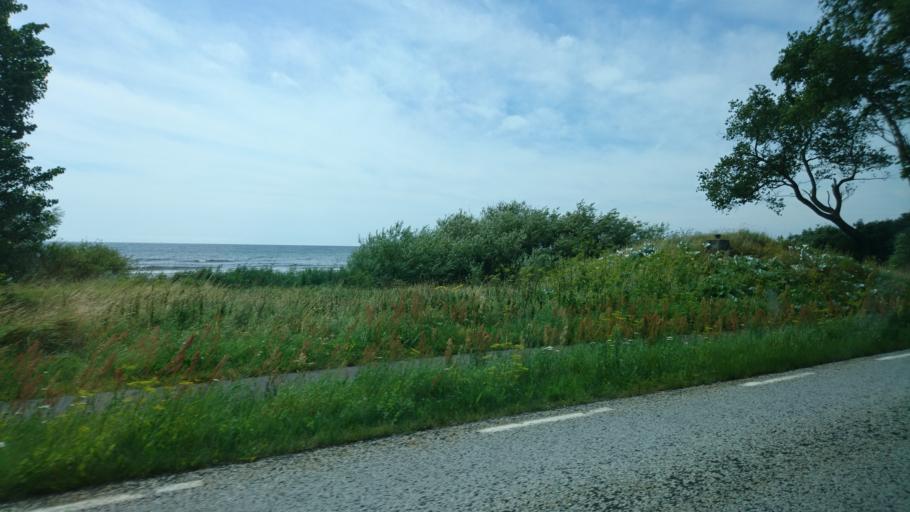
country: SE
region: Skane
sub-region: Skurups Kommun
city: Skivarp
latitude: 55.3880
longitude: 13.5419
